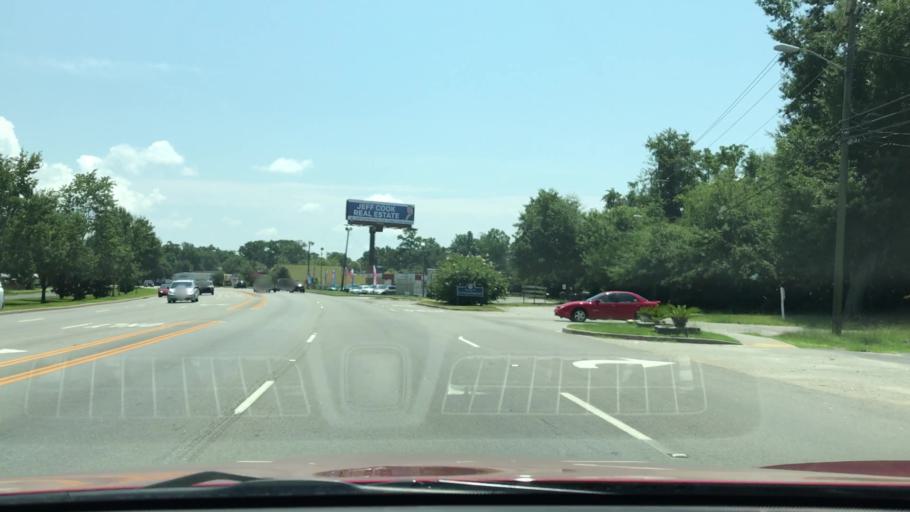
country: US
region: South Carolina
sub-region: Berkeley County
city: Hanahan
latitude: 32.8568
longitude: -80.0432
